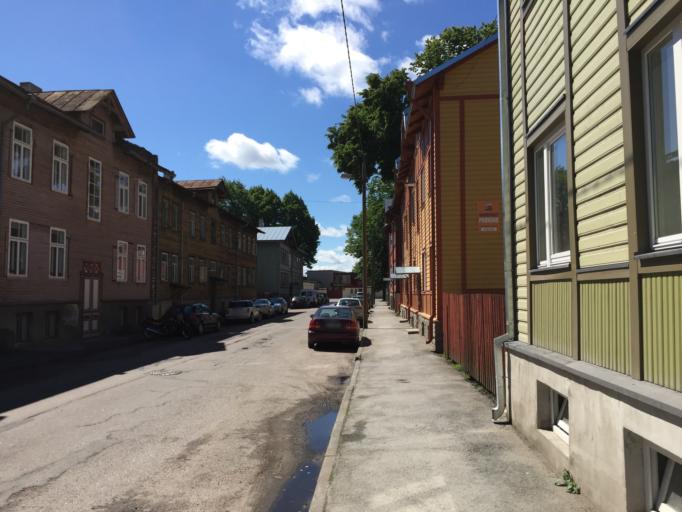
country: EE
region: Harju
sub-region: Tallinna linn
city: Tallinn
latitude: 59.4431
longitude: 24.7293
